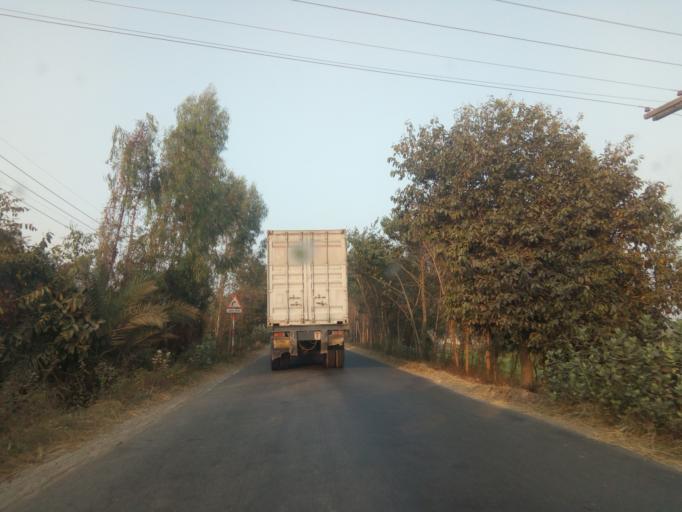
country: BD
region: Rajshahi
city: Bogra
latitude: 24.5514
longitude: 89.1921
